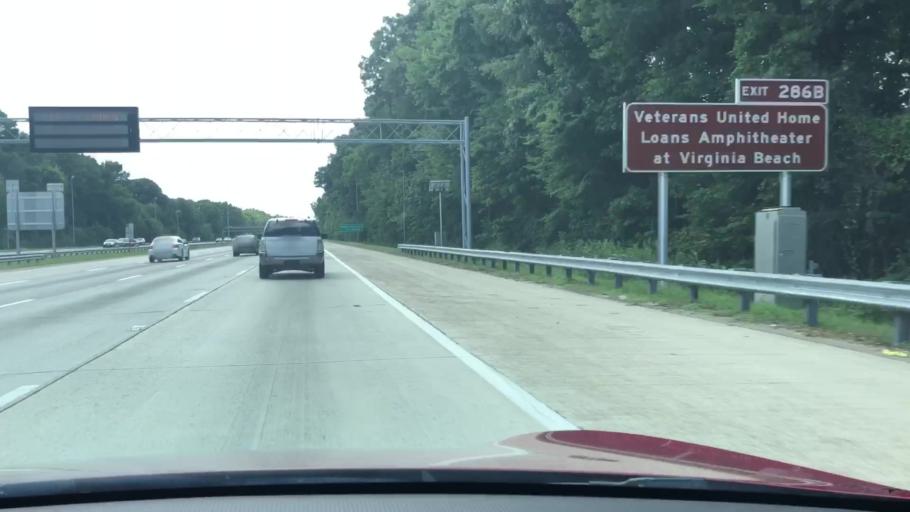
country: US
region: Virginia
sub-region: City of Chesapeake
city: Chesapeake
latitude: 36.8181
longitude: -76.1951
